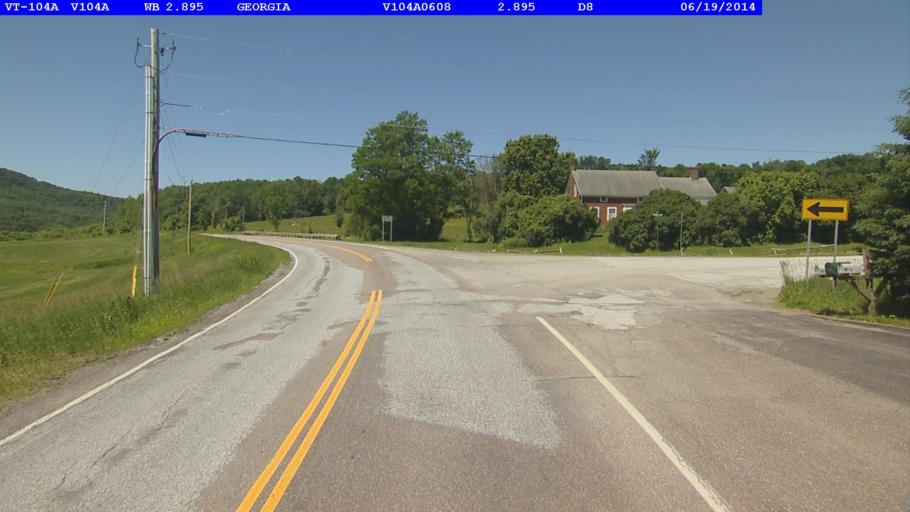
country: US
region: Vermont
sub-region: Chittenden County
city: Milton
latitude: 44.6837
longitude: -73.0598
